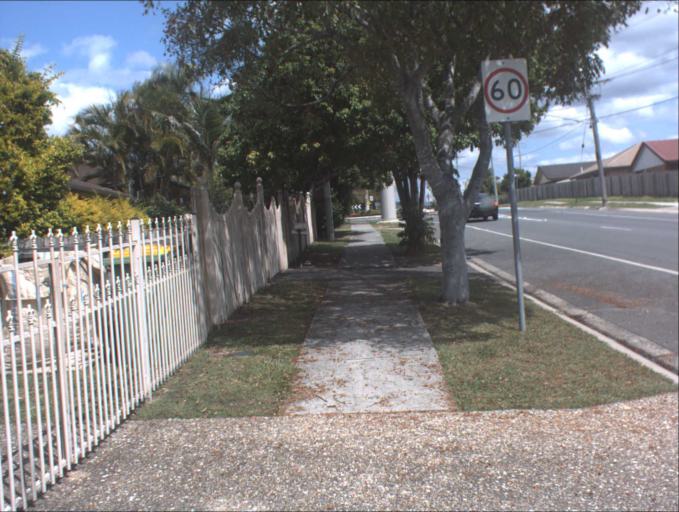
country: AU
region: Queensland
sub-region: Logan
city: Logan City
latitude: -27.6690
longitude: 153.0871
